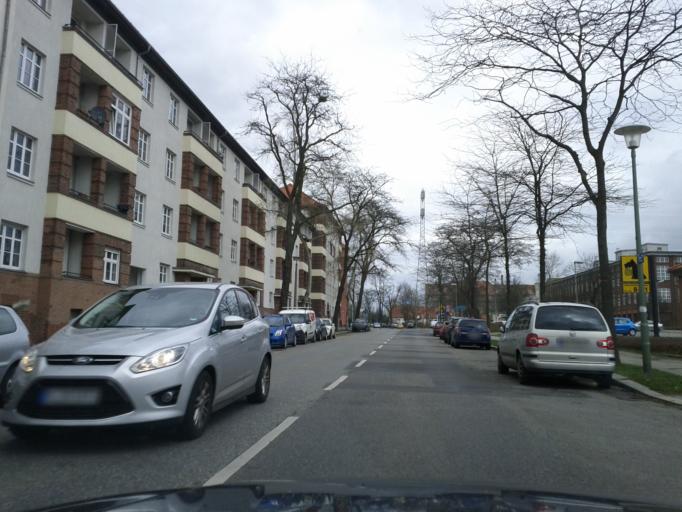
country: DE
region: Berlin
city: Lichtenberg
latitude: 52.5197
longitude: 13.4860
